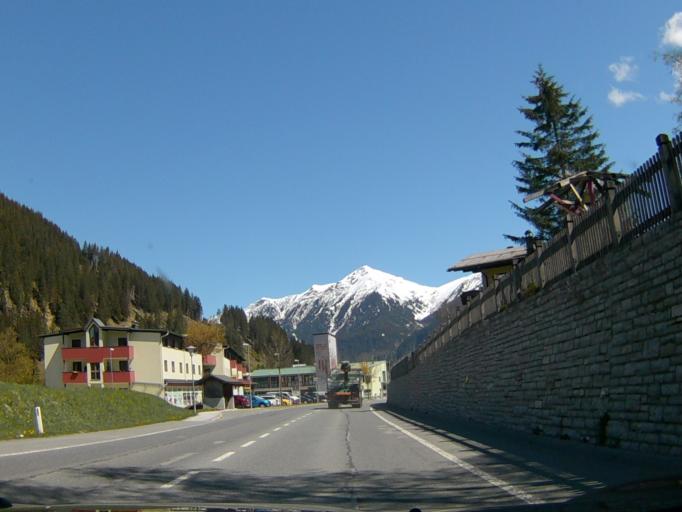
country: AT
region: Salzburg
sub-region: Politischer Bezirk Sankt Johann im Pongau
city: Bad Gastein
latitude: 47.0996
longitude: 13.1267
